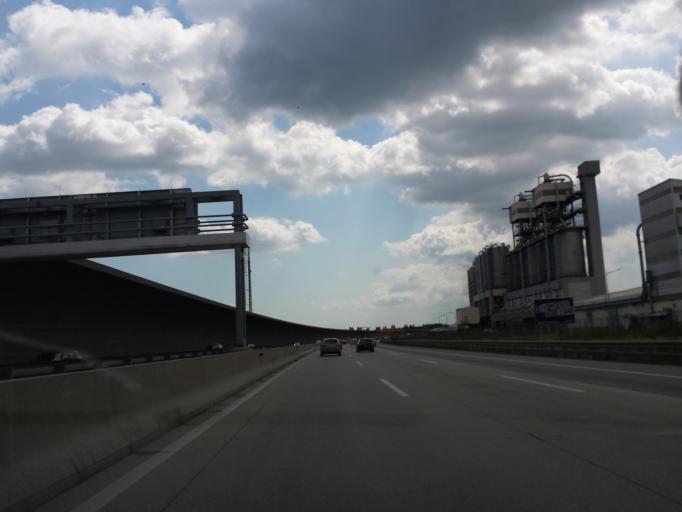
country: AT
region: Lower Austria
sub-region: Politischer Bezirk Wien-Umgebung
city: Schwechat
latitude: 48.1446
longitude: 16.5110
